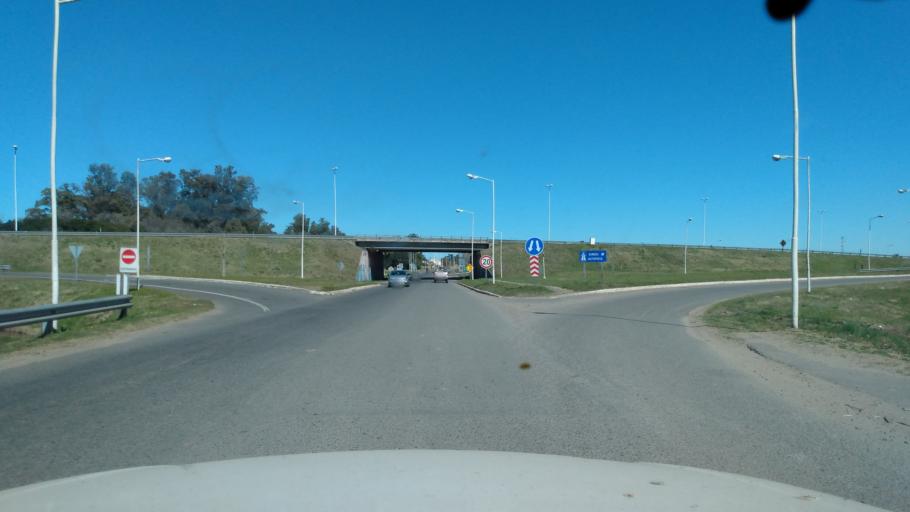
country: AR
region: Buenos Aires
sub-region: Partido de Lujan
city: Lujan
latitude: -34.5556
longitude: -59.0985
